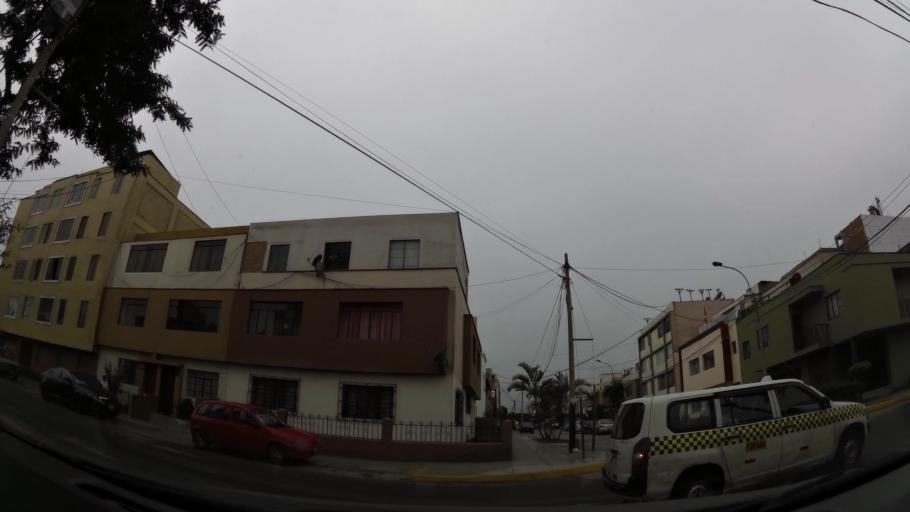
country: PE
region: Lima
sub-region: Lima
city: San Isidro
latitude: -12.0844
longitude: -77.0637
